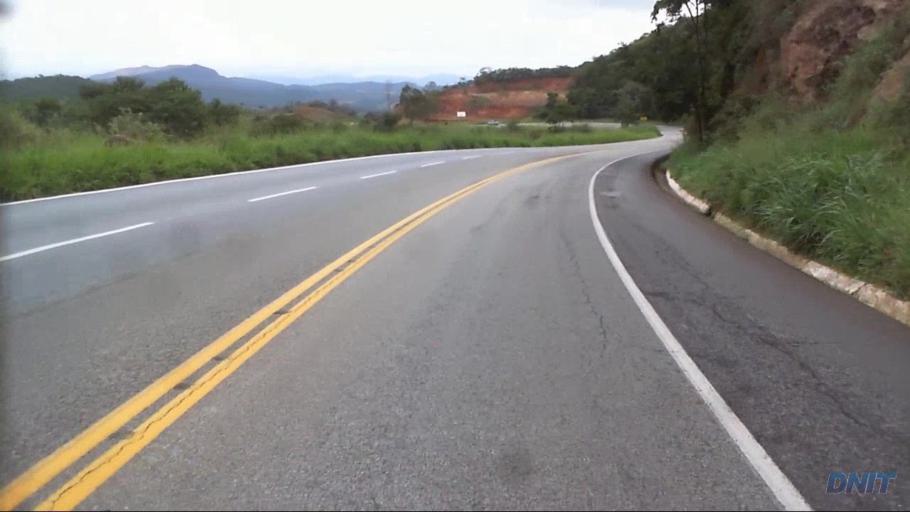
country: BR
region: Minas Gerais
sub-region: Joao Monlevade
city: Joao Monlevade
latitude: -19.8441
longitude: -43.3109
